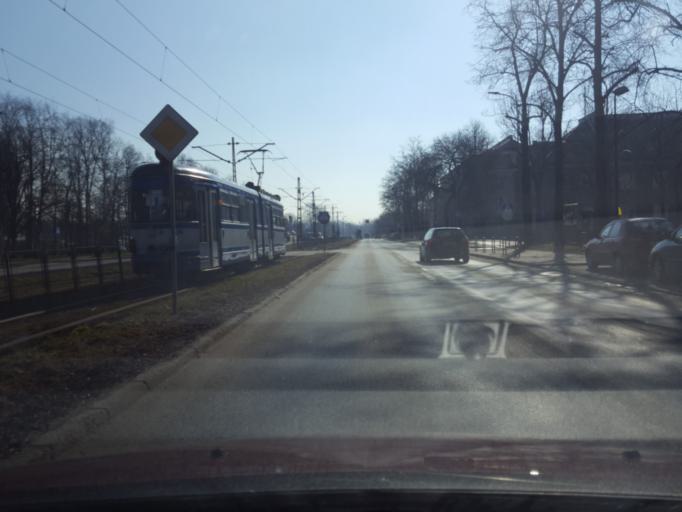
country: PL
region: Lesser Poland Voivodeship
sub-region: Powiat wielicki
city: Kokotow
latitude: 50.0691
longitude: 20.0489
